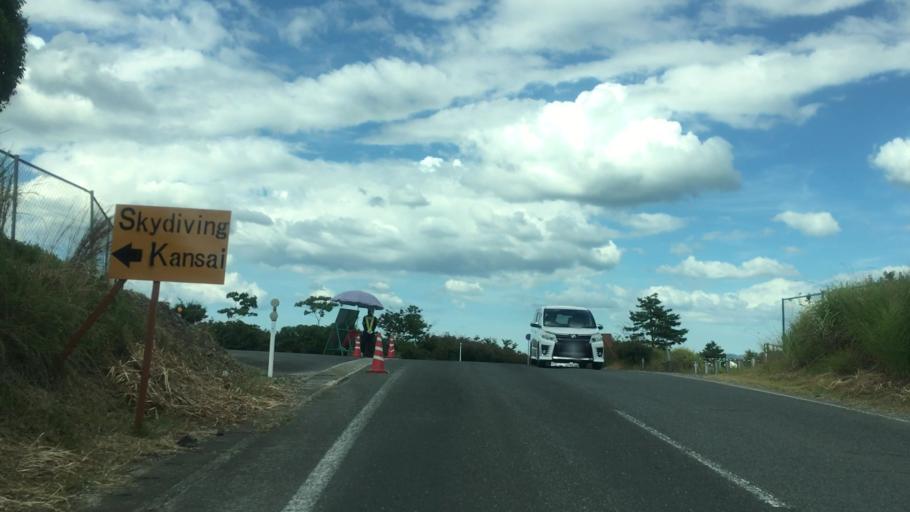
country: JP
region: Hyogo
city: Toyooka
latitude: 35.5150
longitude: 134.7838
